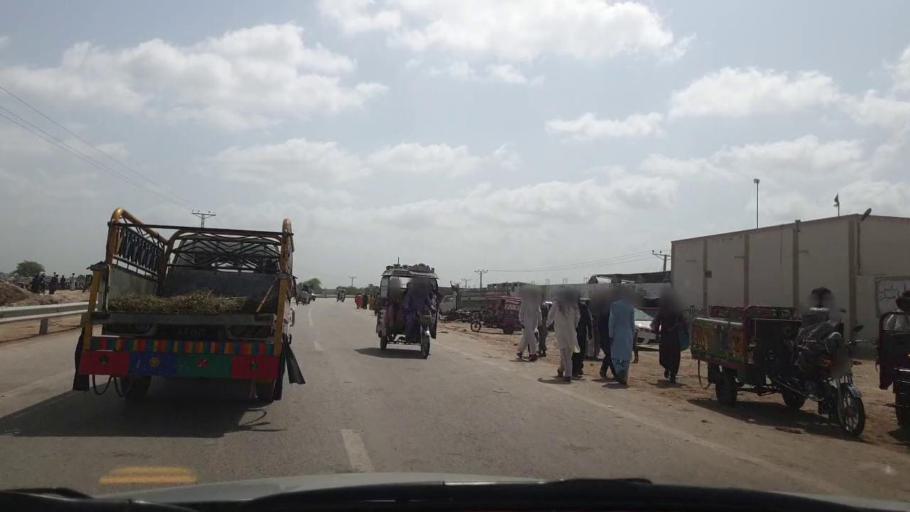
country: PK
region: Sindh
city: Talhar
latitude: 24.8930
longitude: 68.7936
